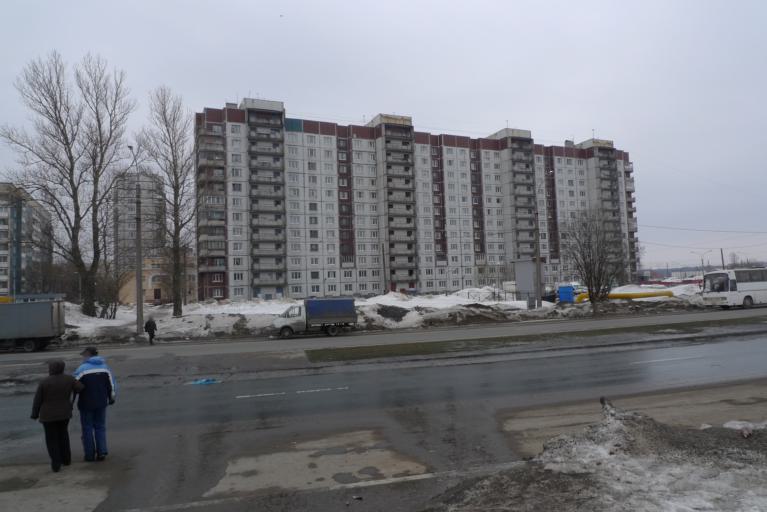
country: RU
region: St.-Petersburg
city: Shuvalovo
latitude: 60.0677
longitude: 30.3044
